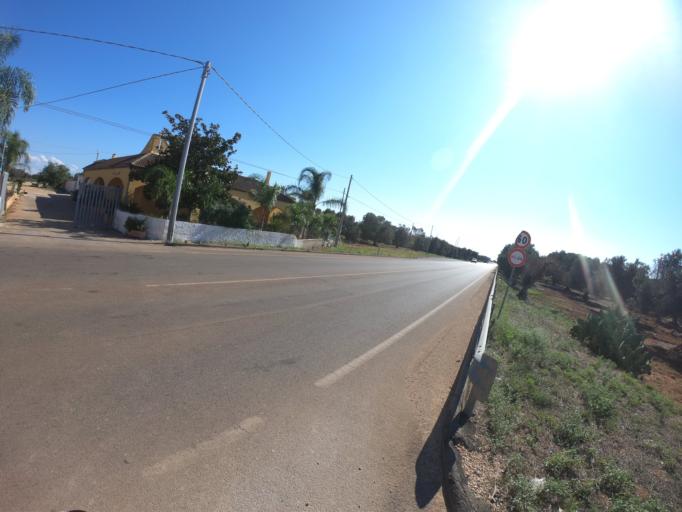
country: IT
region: Apulia
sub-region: Provincia di Lecce
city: Leverano
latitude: 40.2377
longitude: 17.9629
